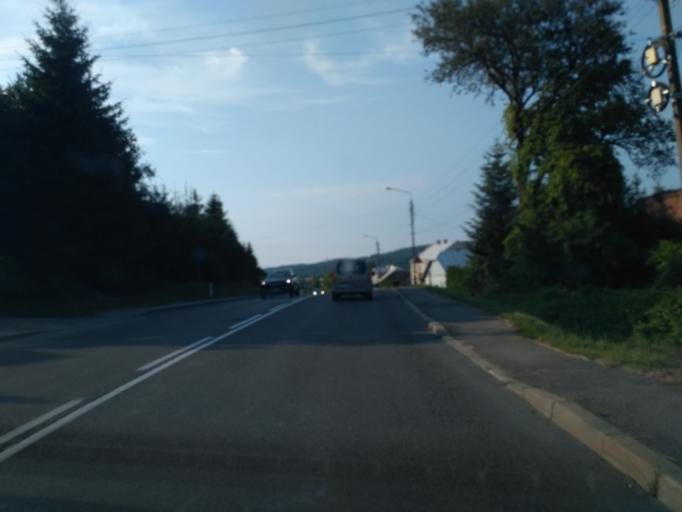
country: PL
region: Subcarpathian Voivodeship
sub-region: Powiat brzozowski
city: Grabownica Starzenska
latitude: 49.6526
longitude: 22.0809
